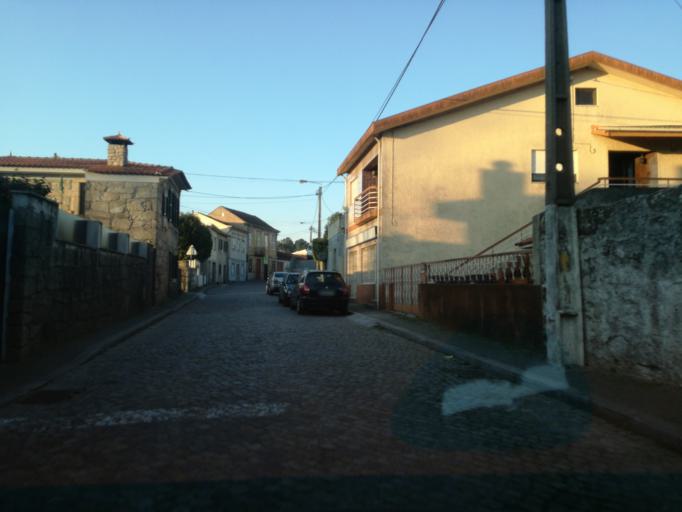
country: PT
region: Porto
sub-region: Maia
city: Milheiros
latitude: 41.2178
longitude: -8.5920
